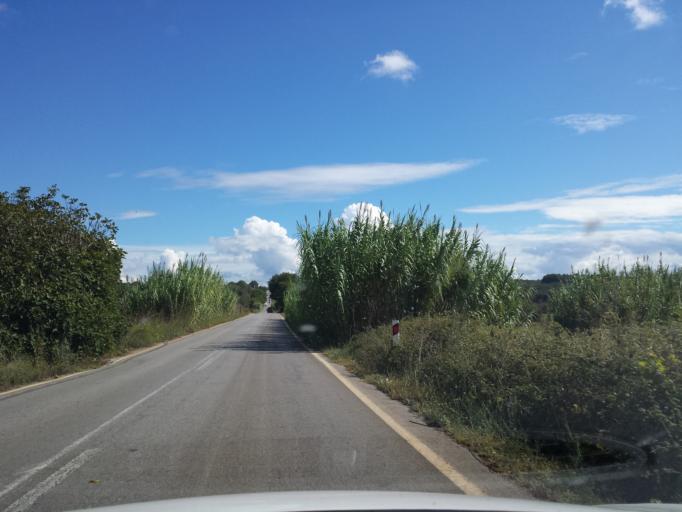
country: GR
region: Peloponnese
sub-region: Nomos Messinias
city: Vlakhopoulon
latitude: 36.9862
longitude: 21.8275
